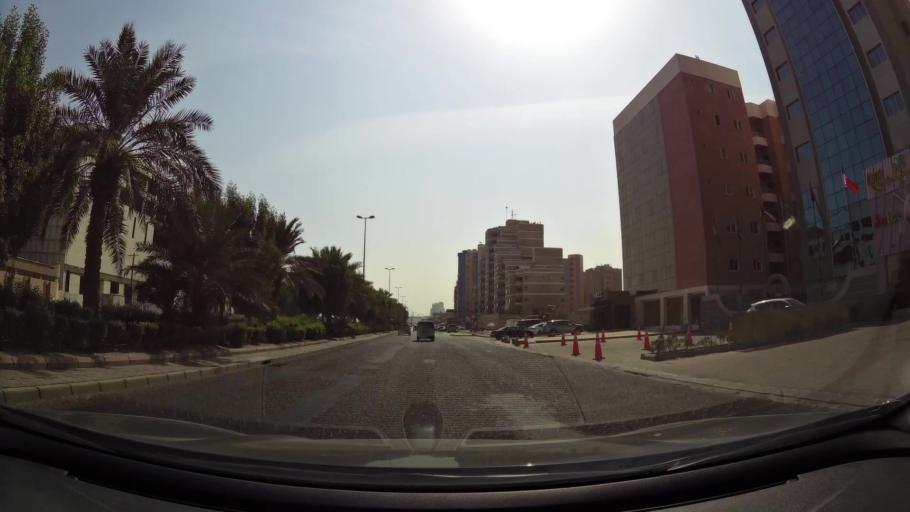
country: KW
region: Al Ahmadi
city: Al Manqaf
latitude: 29.0958
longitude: 48.1373
